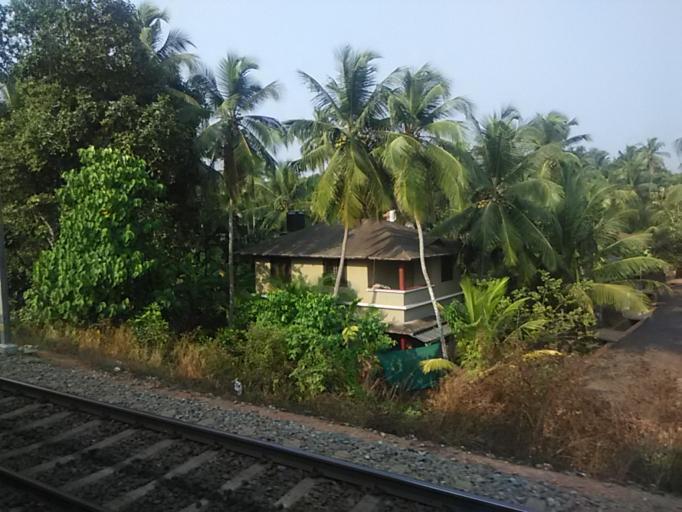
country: IN
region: Kerala
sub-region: Malappuram
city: Pariyapuram
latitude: 11.0391
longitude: 75.8643
